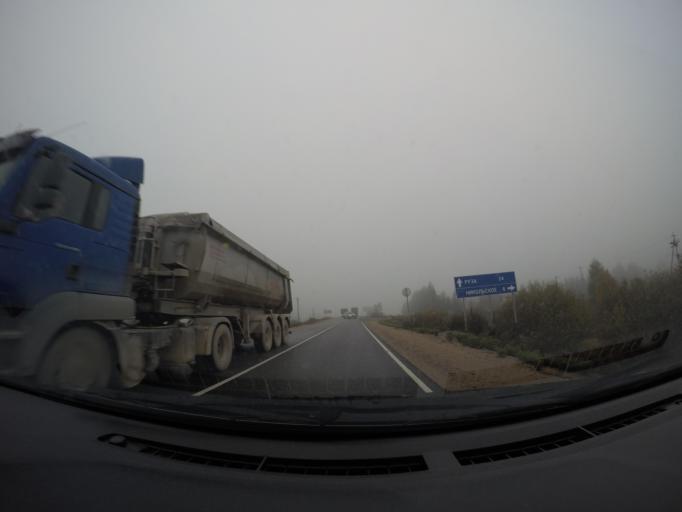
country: RU
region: Moskovskaya
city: Novopetrovskoye
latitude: 55.8358
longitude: 36.4518
